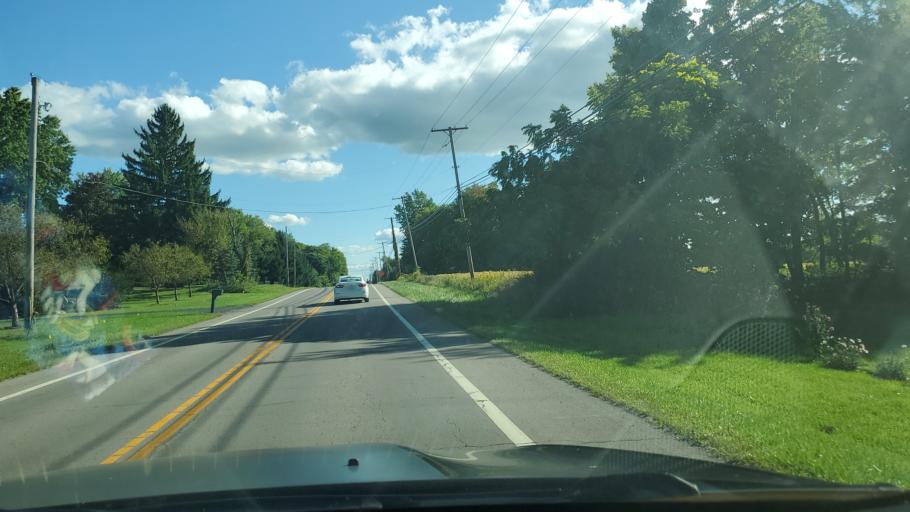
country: US
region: Ohio
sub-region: Mahoning County
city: Canfield
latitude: 41.0495
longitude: -80.7607
